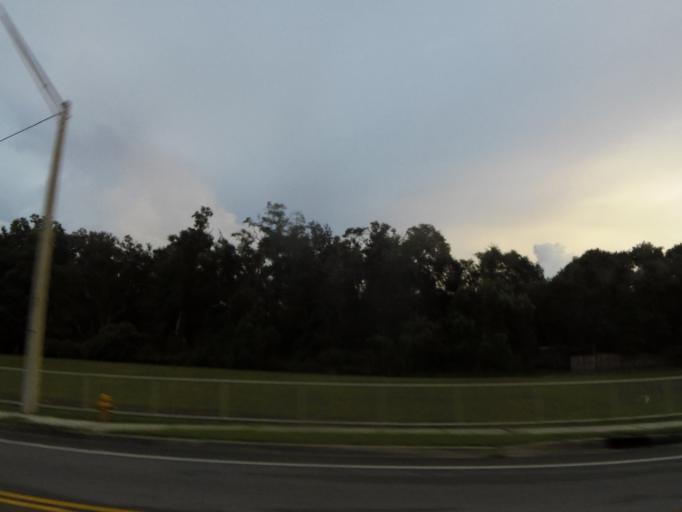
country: US
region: Florida
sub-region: Duval County
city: Jacksonville
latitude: 30.3668
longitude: -81.5591
